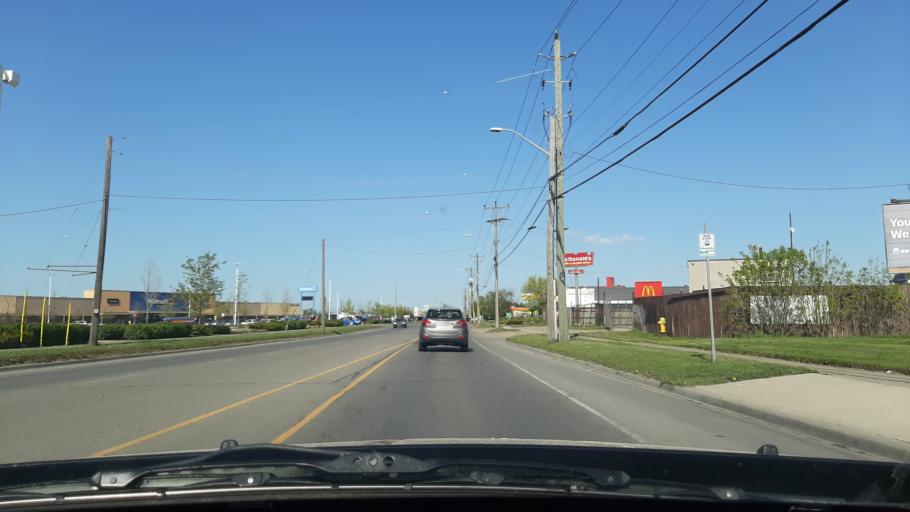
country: CA
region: Ontario
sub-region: Regional Municipality of Niagara
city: St. Catharines
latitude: 43.1750
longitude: -79.2143
